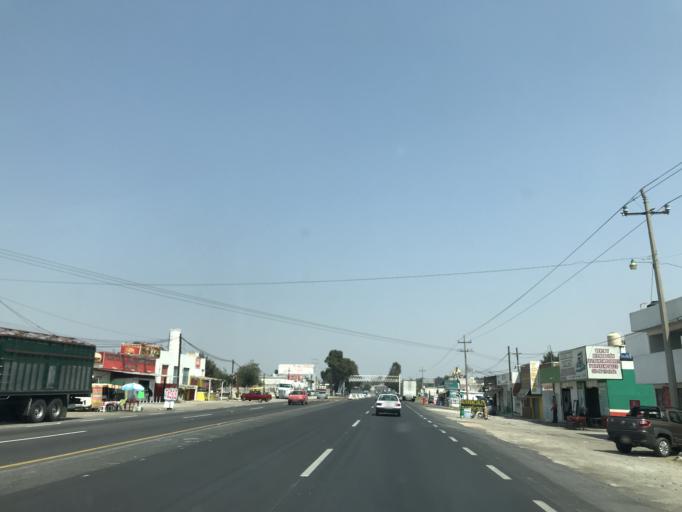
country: MX
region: Tlaxcala
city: Yauhquemehcan
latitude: 19.3950
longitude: -98.1796
